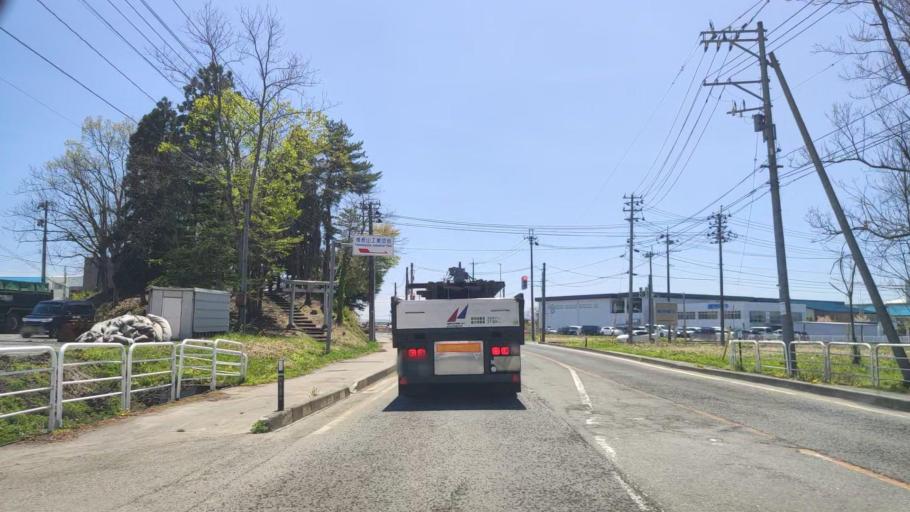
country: JP
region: Yamagata
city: Shinjo
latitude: 38.8227
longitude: 140.3265
